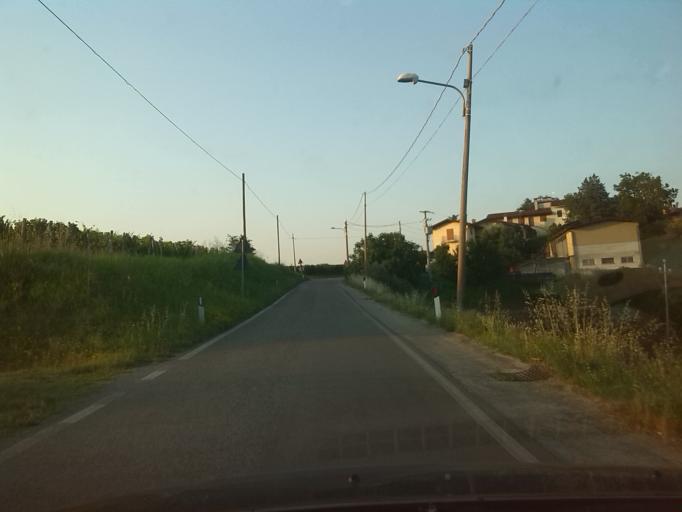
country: SI
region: Brda
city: Dobrovo
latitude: 45.9798
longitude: 13.4972
